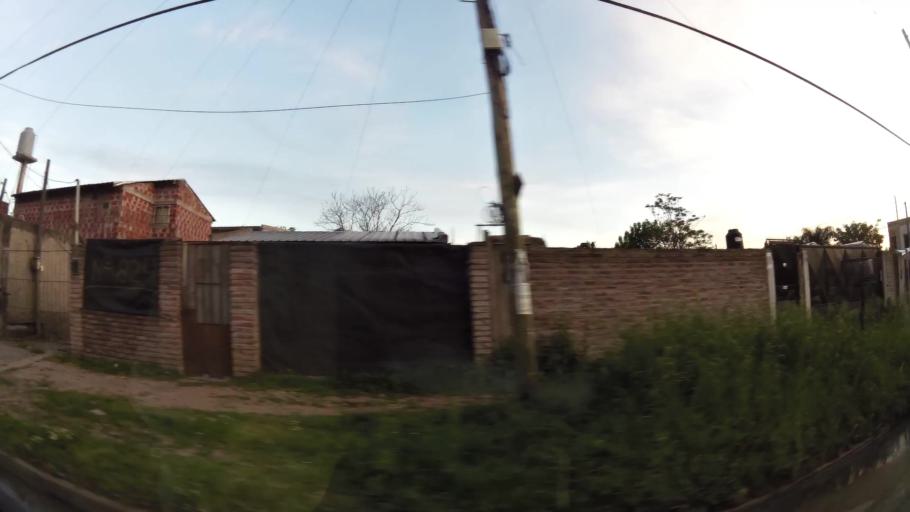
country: AR
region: Buenos Aires
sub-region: Partido de Quilmes
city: Quilmes
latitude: -34.8005
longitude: -58.2898
